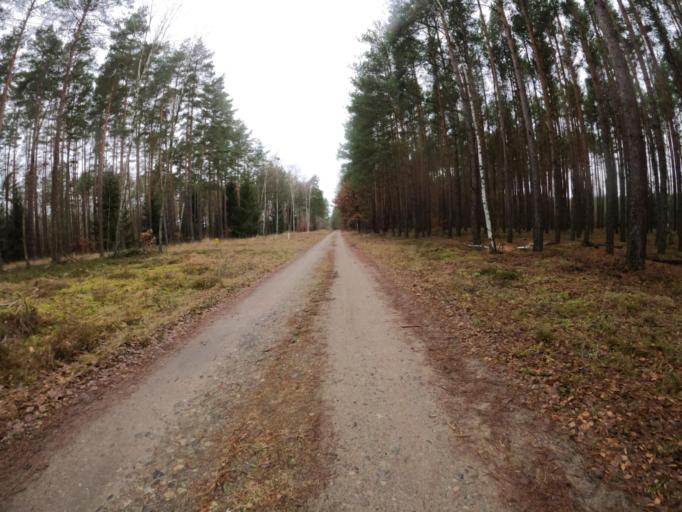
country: PL
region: West Pomeranian Voivodeship
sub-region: Powiat mysliborski
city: Debno
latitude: 52.7557
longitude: 14.7697
